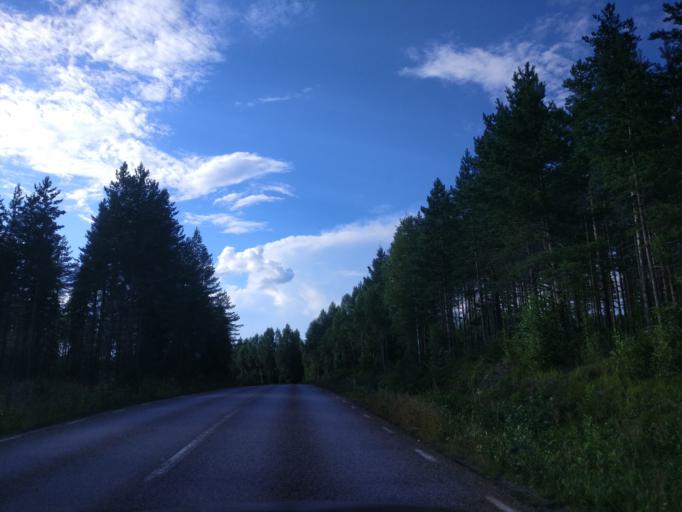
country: SE
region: Dalarna
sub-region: Ludvika Kommun
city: Ludvika
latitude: 60.2905
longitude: 15.1355
